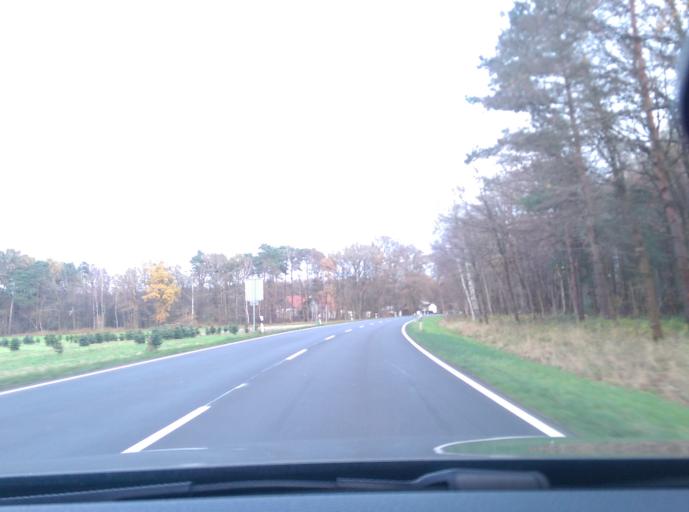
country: DE
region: Lower Saxony
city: Hambuhren
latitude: 52.6043
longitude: 9.9926
